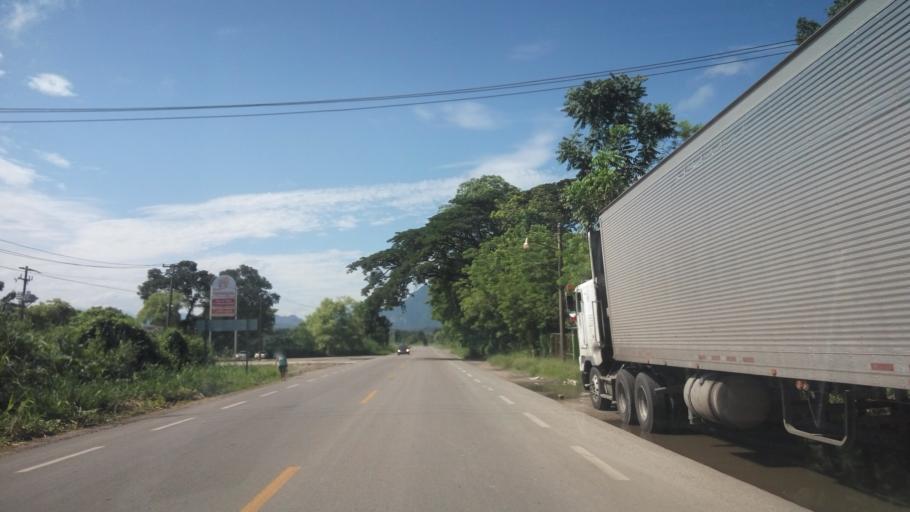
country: MX
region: Tabasco
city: Teapa
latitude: 17.5901
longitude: -92.9661
